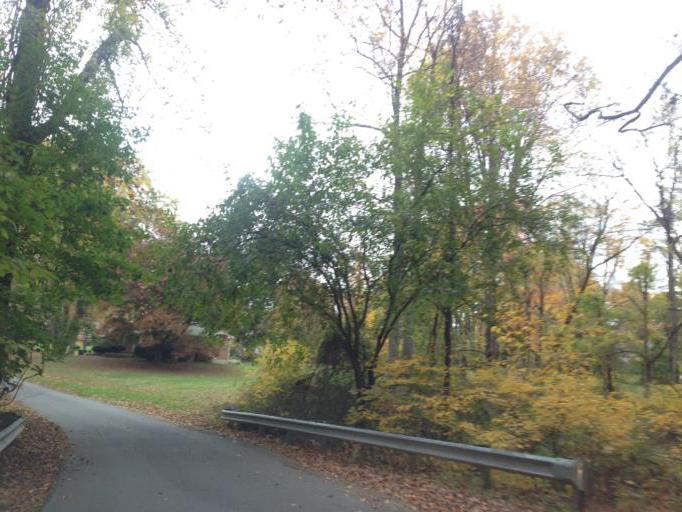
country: US
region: Maryland
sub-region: Baltimore County
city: Randallstown
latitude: 39.3903
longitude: -76.8595
